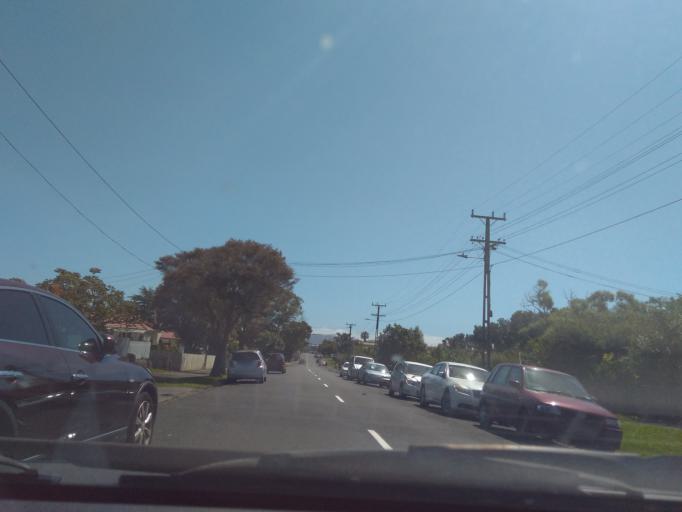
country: NZ
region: Auckland
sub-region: Auckland
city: Rosebank
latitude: -36.8991
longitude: 174.6948
